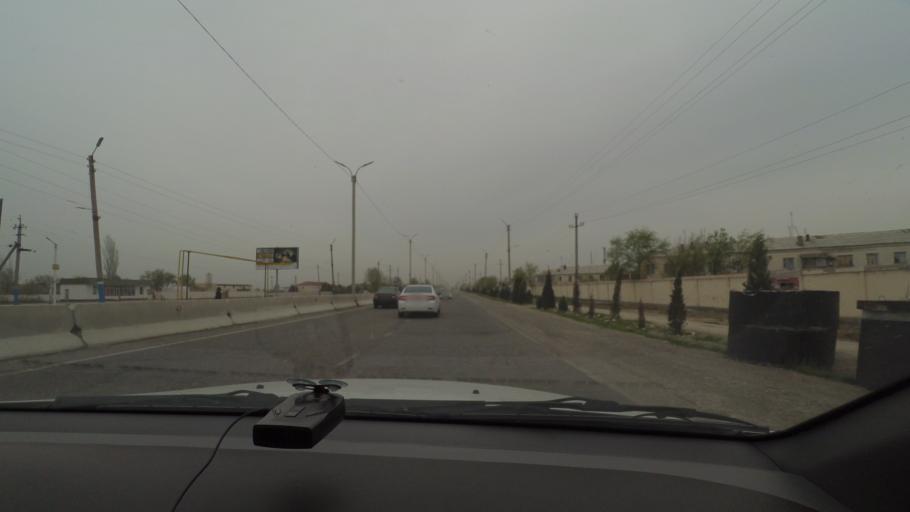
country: KZ
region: Ongtustik Qazaqstan
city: Myrzakent
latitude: 40.5443
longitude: 68.4135
